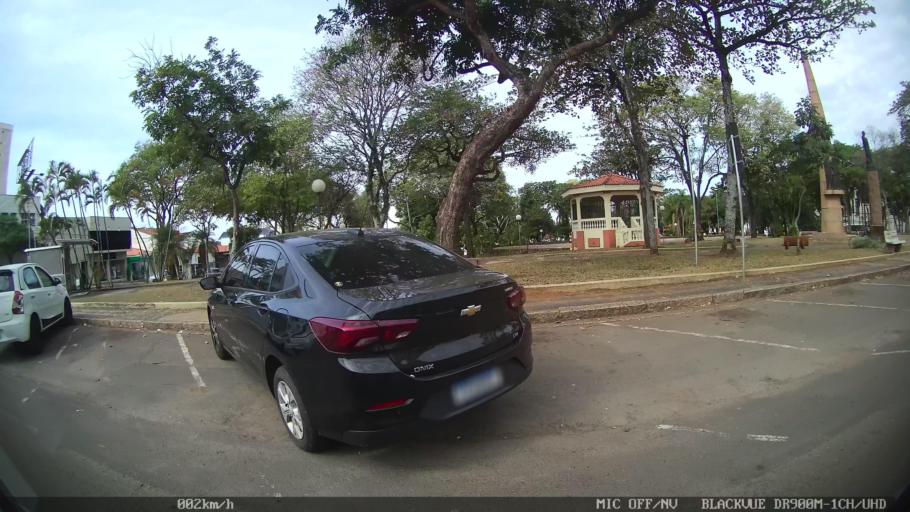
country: BR
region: Sao Paulo
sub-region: Piracicaba
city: Piracicaba
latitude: -22.7123
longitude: -47.6549
